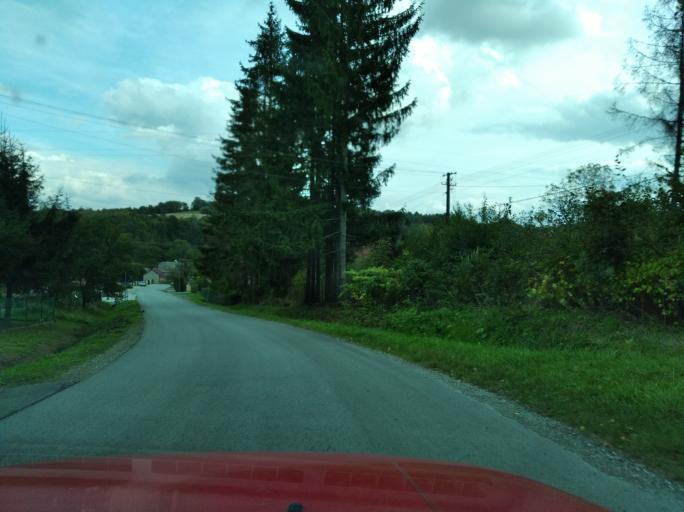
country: PL
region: Subcarpathian Voivodeship
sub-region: Powiat rzeszowski
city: Tyczyn
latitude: 49.9320
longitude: 22.0156
